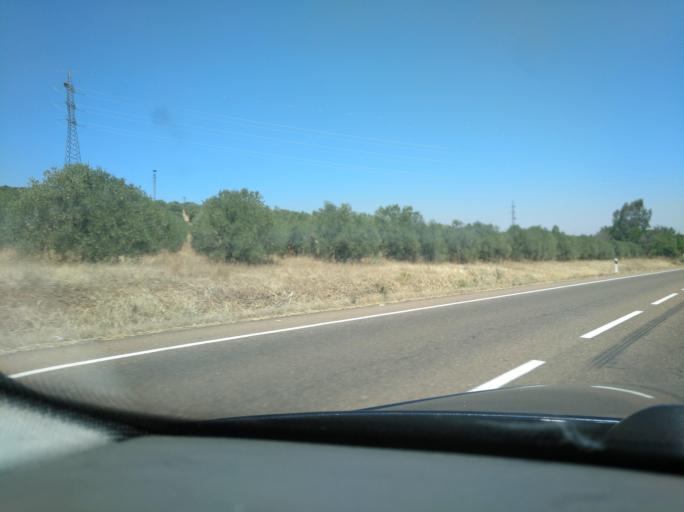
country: ES
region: Extremadura
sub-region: Provincia de Badajoz
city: Olivenza
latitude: 38.7343
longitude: -7.0689
